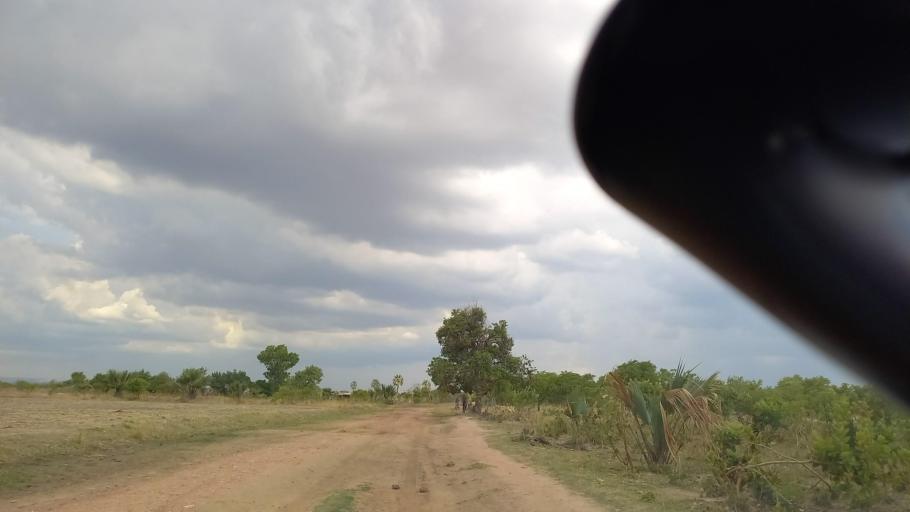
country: ZM
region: Lusaka
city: Kafue
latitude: -15.8356
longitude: 28.0777
